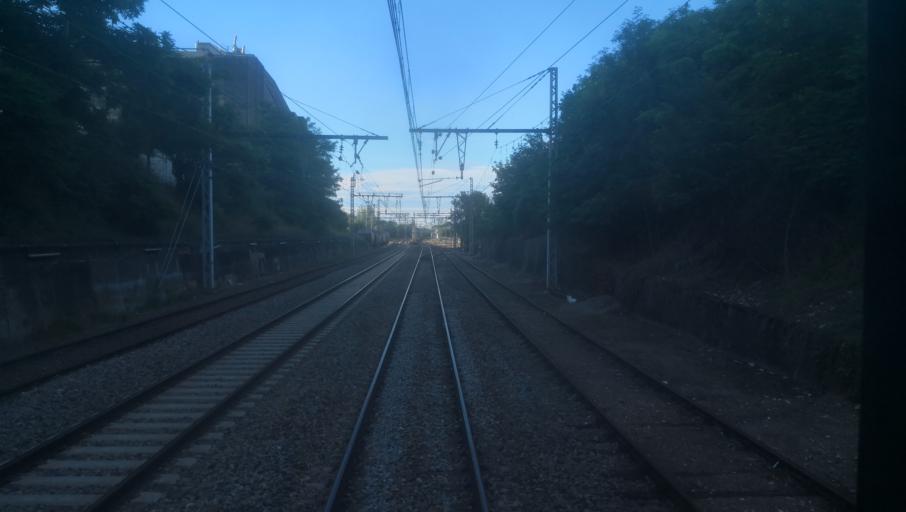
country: FR
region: Centre
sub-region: Departement de l'Indre
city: Issoudun
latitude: 46.9438
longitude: 1.9827
